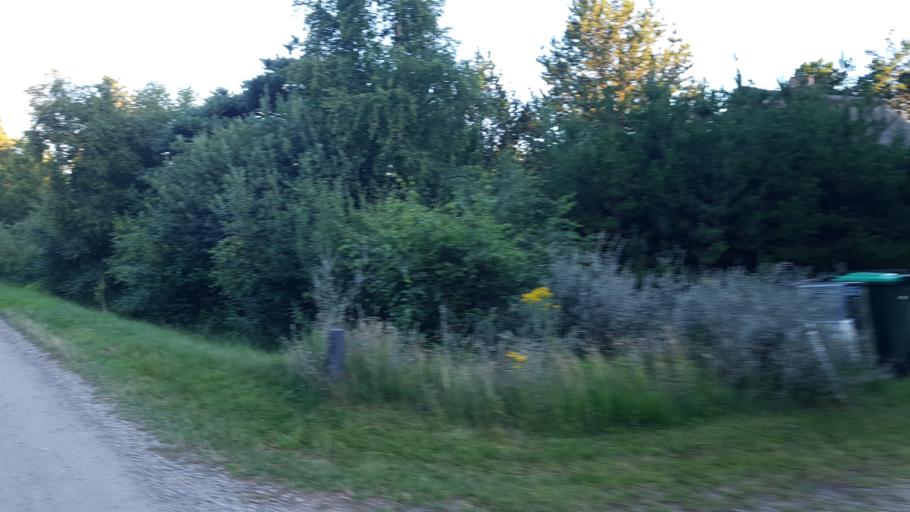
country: DE
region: Schleswig-Holstein
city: List
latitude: 55.0915
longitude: 8.5264
